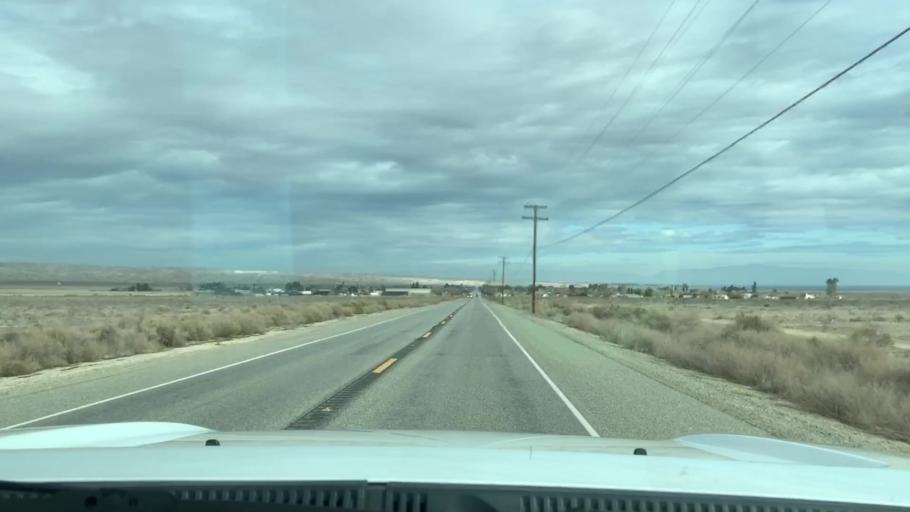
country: US
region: California
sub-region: Kern County
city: Ford City
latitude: 35.2001
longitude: -119.4199
